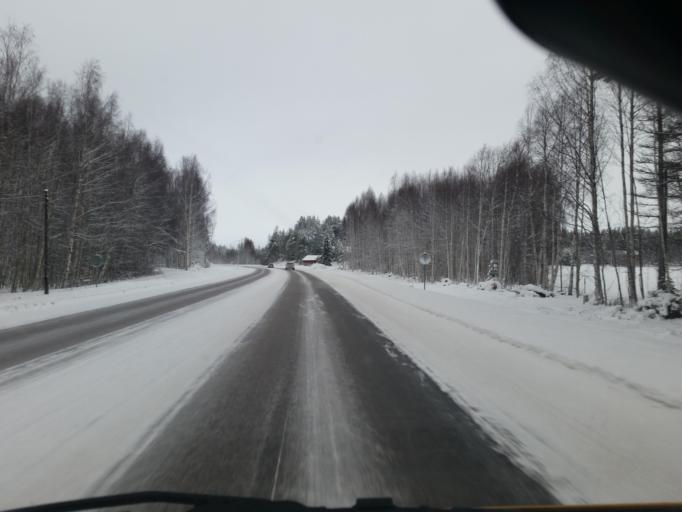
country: SE
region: Norrbotten
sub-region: Pitea Kommun
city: Bergsviken
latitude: 65.3150
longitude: 21.3952
